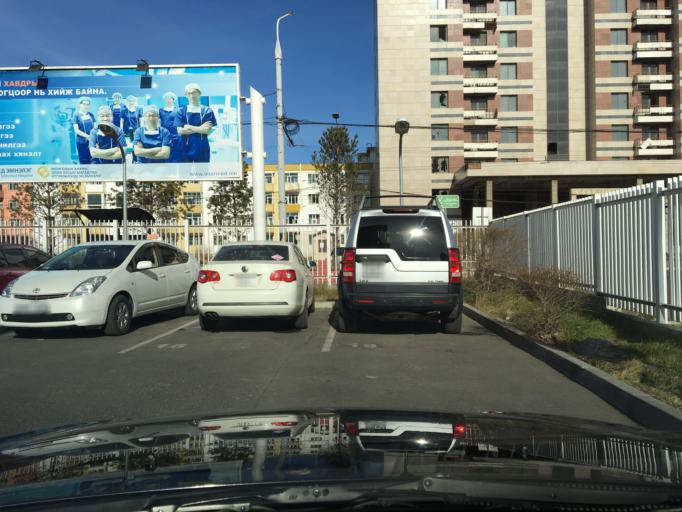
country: MN
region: Ulaanbaatar
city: Ulaanbaatar
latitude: 47.8988
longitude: 106.9056
